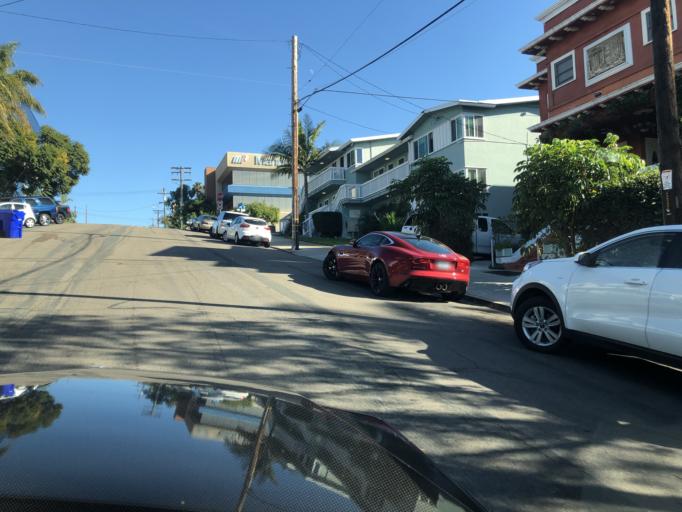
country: US
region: California
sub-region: San Diego County
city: San Diego
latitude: 32.7251
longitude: -117.1646
